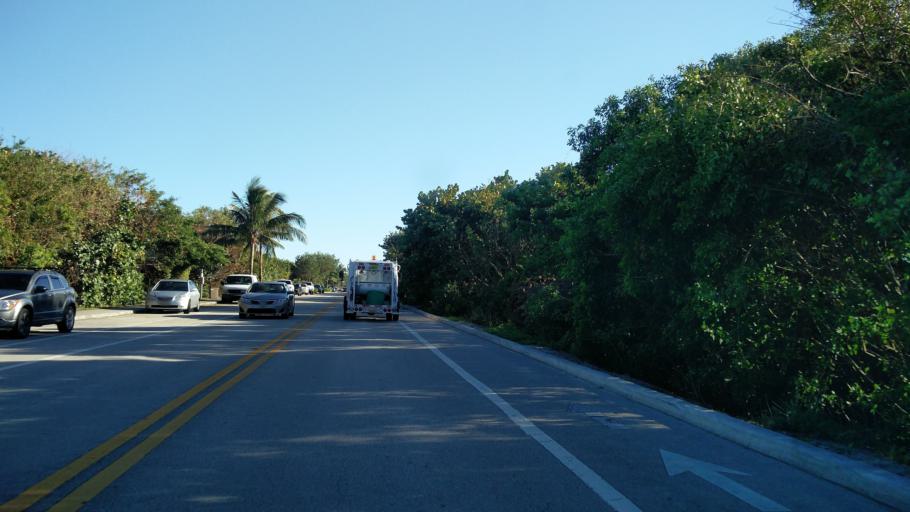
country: US
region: Florida
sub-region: Palm Beach County
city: Juno Beach
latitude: 26.9104
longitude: -80.0630
